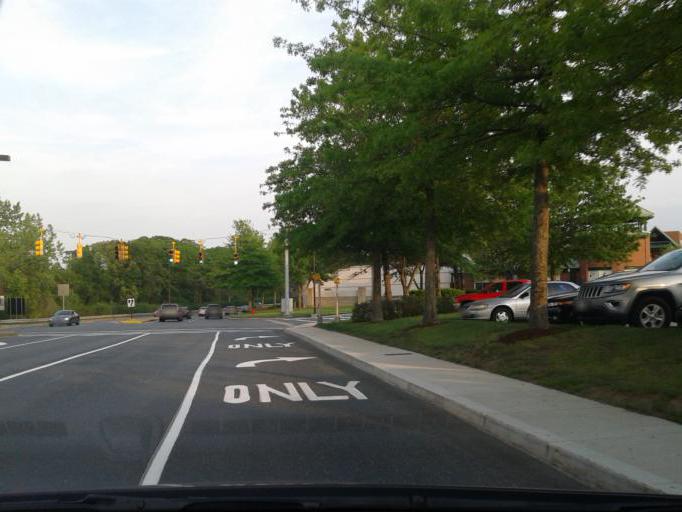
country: US
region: Massachusetts
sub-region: Middlesex County
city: Framingham
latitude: 42.3038
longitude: -71.3941
